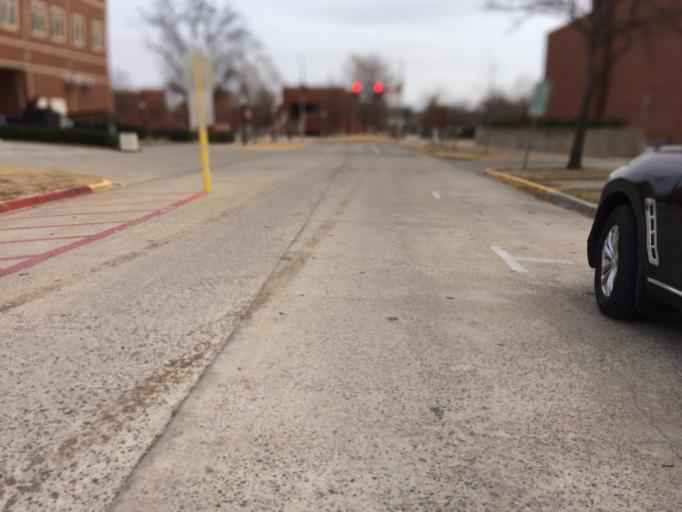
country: US
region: Oklahoma
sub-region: Cleveland County
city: Norman
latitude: 35.2098
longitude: -97.4421
